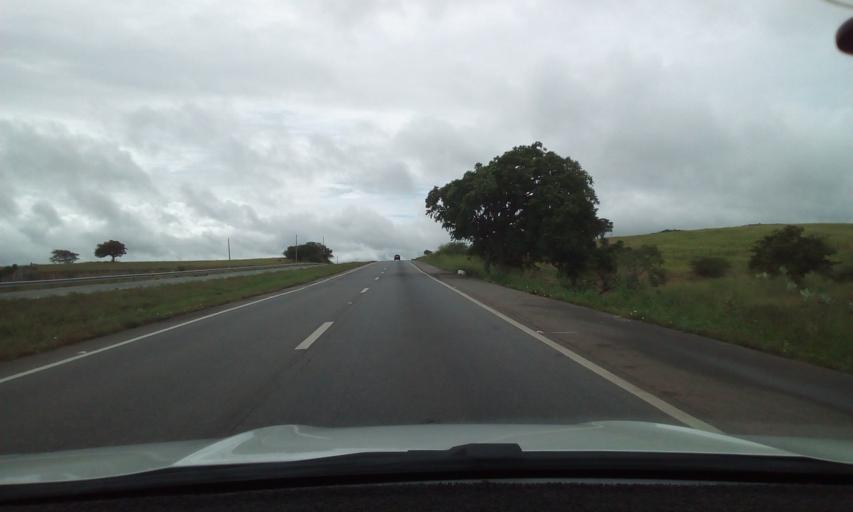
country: BR
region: Paraiba
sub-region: Gurinhem
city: Gurinhem
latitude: -7.1871
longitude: -35.4545
